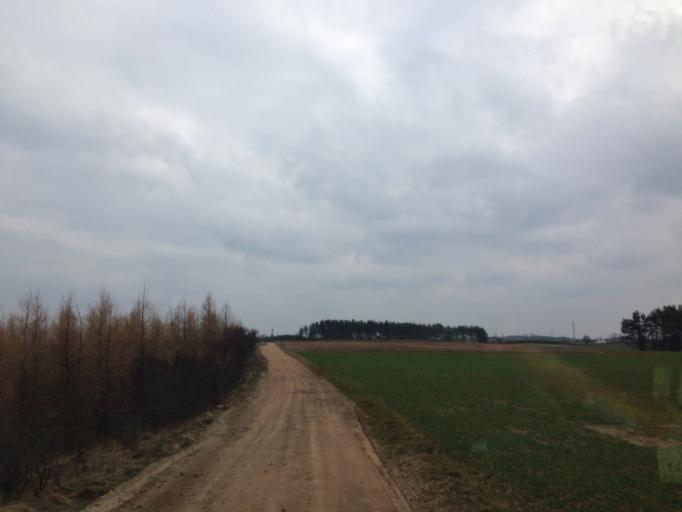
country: PL
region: Warmian-Masurian Voivodeship
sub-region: Powiat dzialdowski
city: Lidzbark
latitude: 53.3678
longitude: 19.7619
